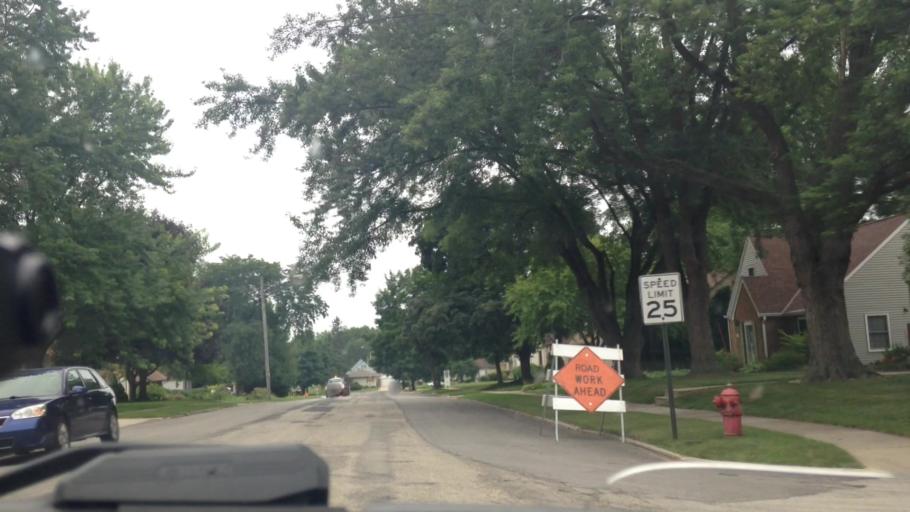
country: US
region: Wisconsin
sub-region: Waukesha County
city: Menomonee Falls
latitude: 43.1774
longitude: -88.1211
